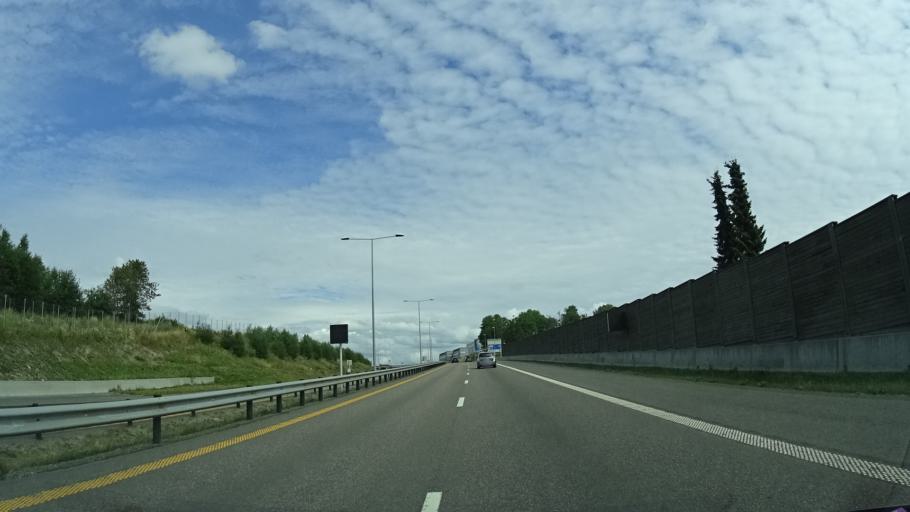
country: NO
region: Vestfold
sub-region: Sandefjord
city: Sandefjord
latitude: 59.1714
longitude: 10.2059
